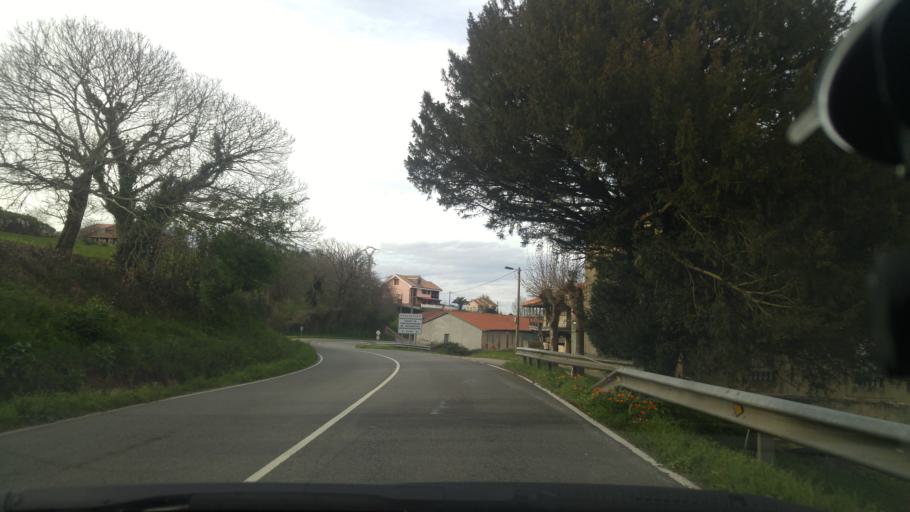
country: ES
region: Asturias
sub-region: Province of Asturias
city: Corvera de Asturias
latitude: 43.4671
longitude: -5.8468
